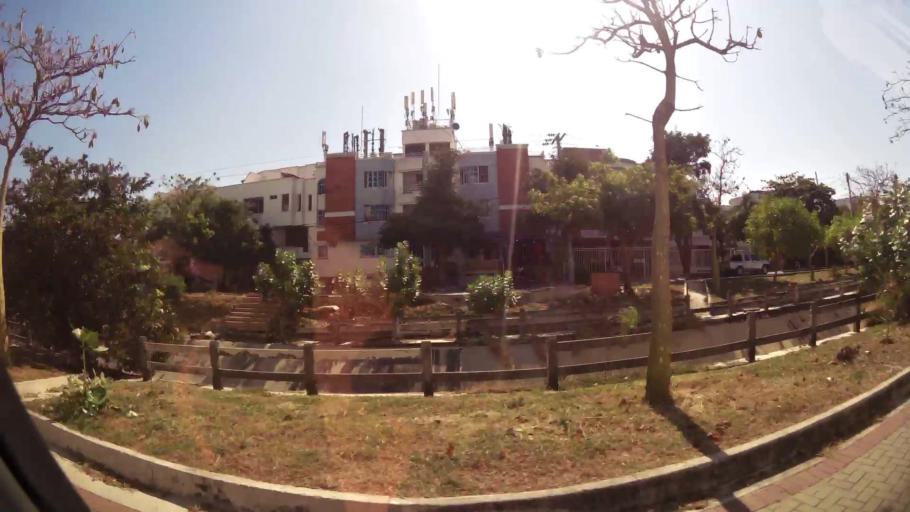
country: CO
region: Atlantico
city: Barranquilla
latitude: 11.0209
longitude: -74.8153
